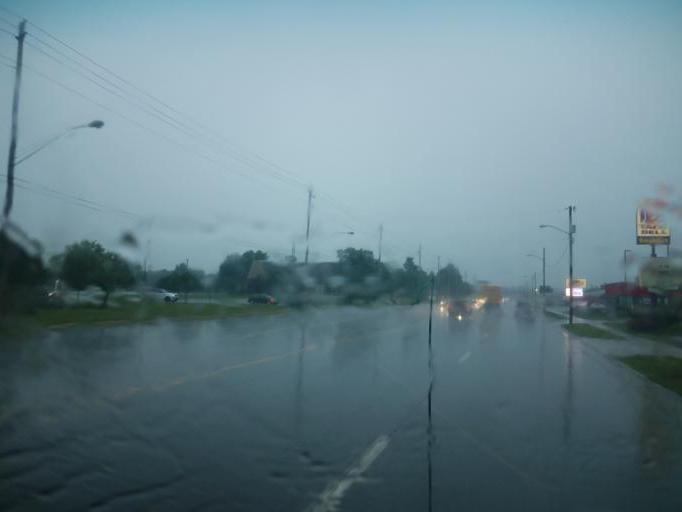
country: US
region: Ohio
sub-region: Stark County
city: Genoa
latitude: 40.7943
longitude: -81.4383
